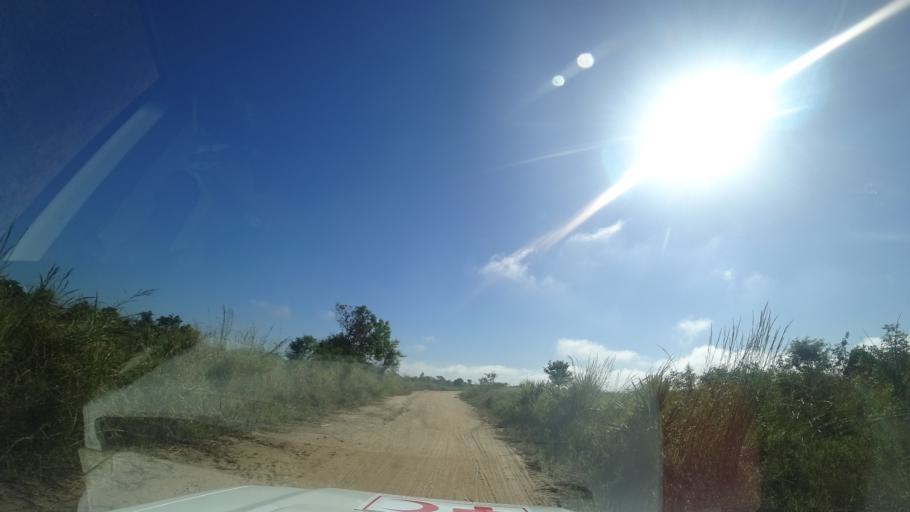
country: MZ
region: Sofala
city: Dondo
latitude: -19.4241
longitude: 34.5625
